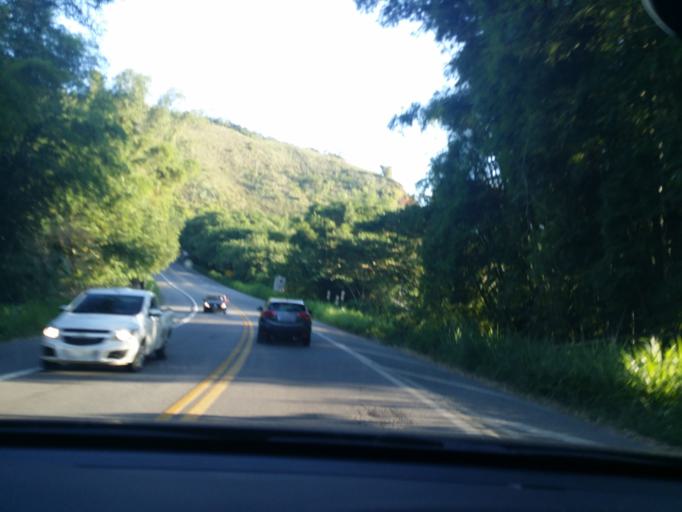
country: BR
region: Sao Paulo
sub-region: Sao Sebastiao
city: Sao Sebastiao
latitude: -23.7670
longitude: -45.7207
